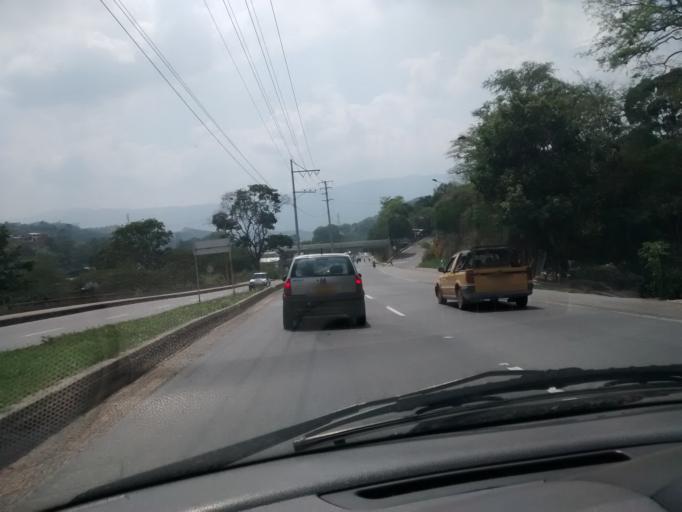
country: CO
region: Santander
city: Bucaramanga
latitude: 7.0929
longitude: -73.1228
